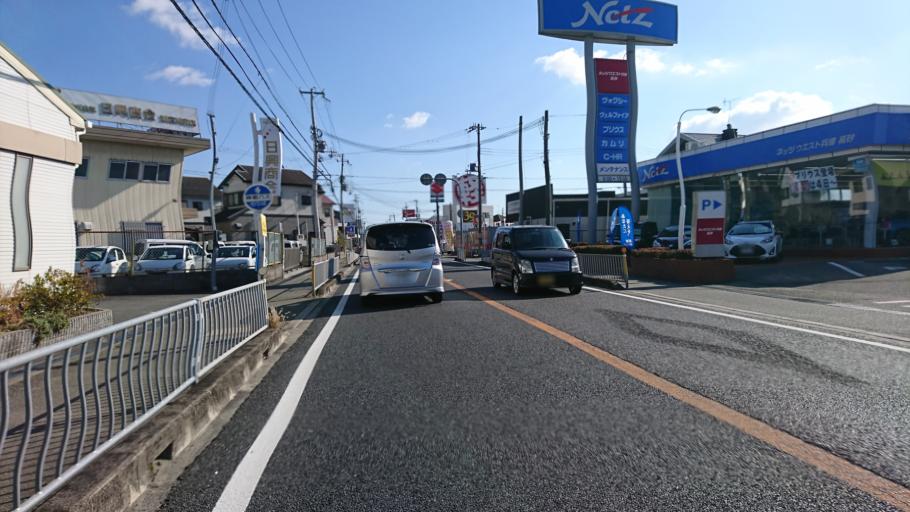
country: JP
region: Hyogo
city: Kakogawacho-honmachi
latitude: 34.7793
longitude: 134.8191
